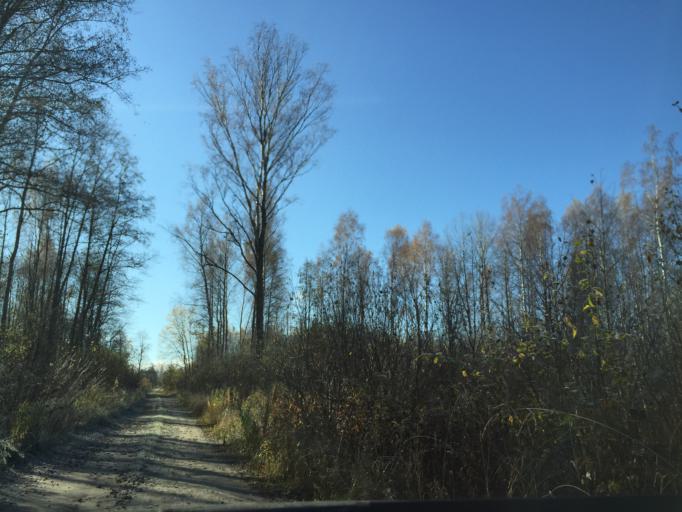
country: LV
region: Aizkraukles Rajons
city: Aizkraukle
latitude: 56.7119
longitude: 25.3006
